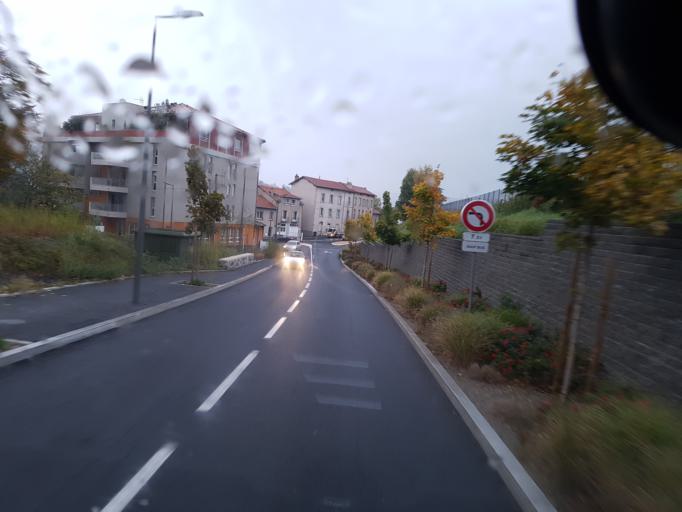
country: FR
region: Auvergne
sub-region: Departement de la Haute-Loire
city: Le Puy-en-Velay
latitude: 45.0464
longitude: 3.8968
